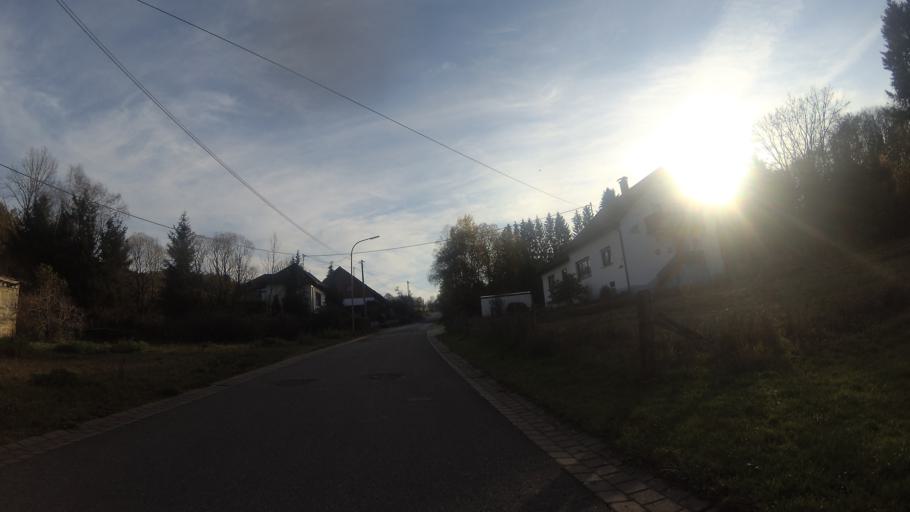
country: DE
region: Rheinland-Pfalz
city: Hahnweiler
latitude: 49.5508
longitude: 7.2033
